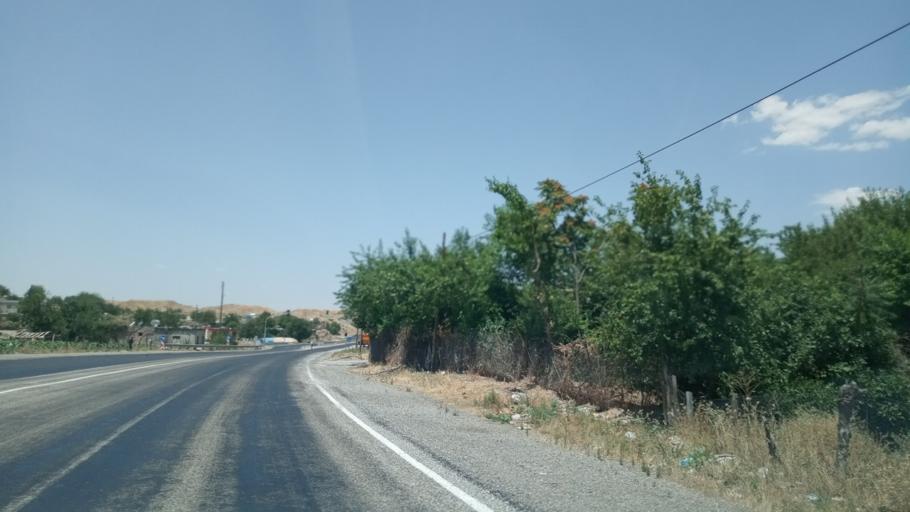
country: TR
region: Batman
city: Kozluk
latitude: 38.1484
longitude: 41.3944
